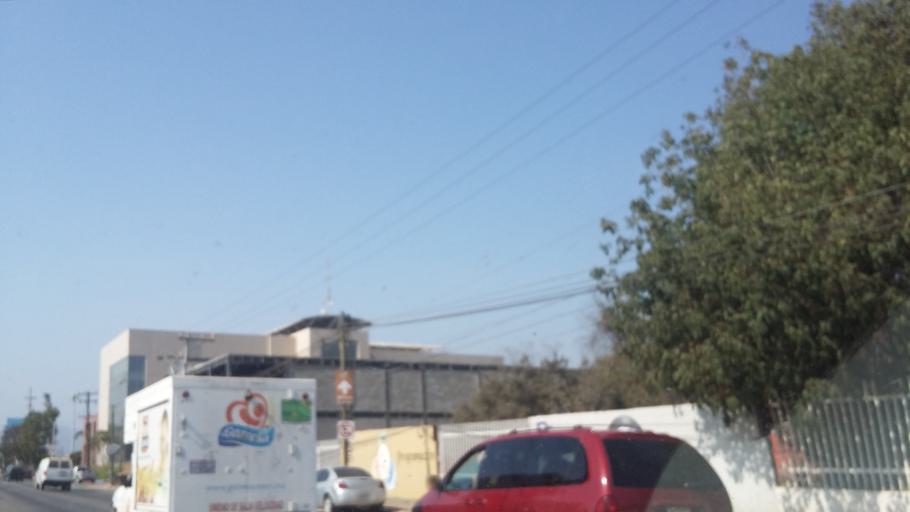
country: MX
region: Baja California
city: Ensenada
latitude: 31.8065
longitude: -116.5959
